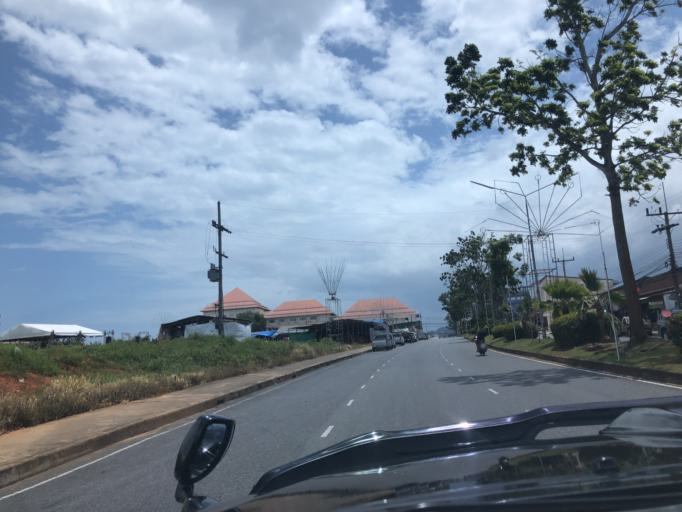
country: TH
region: Krabi
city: Krabi
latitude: 8.0854
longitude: 98.9098
